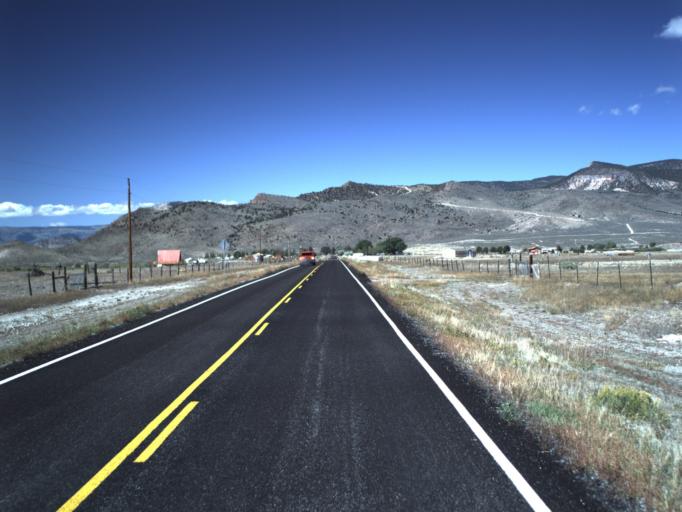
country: US
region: Utah
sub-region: Piute County
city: Junction
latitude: 38.1591
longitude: -112.0064
